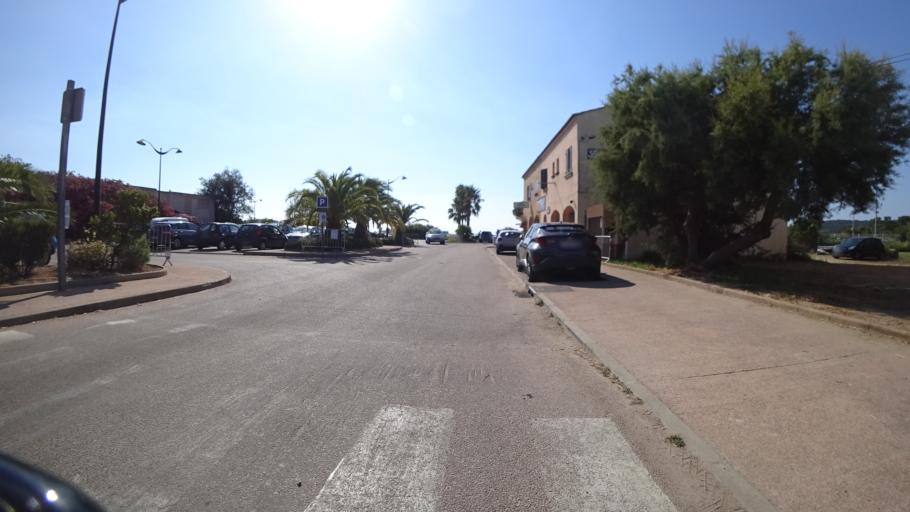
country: FR
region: Corsica
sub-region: Departement de la Corse-du-Sud
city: Porto-Vecchio
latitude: 41.6381
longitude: 9.3470
